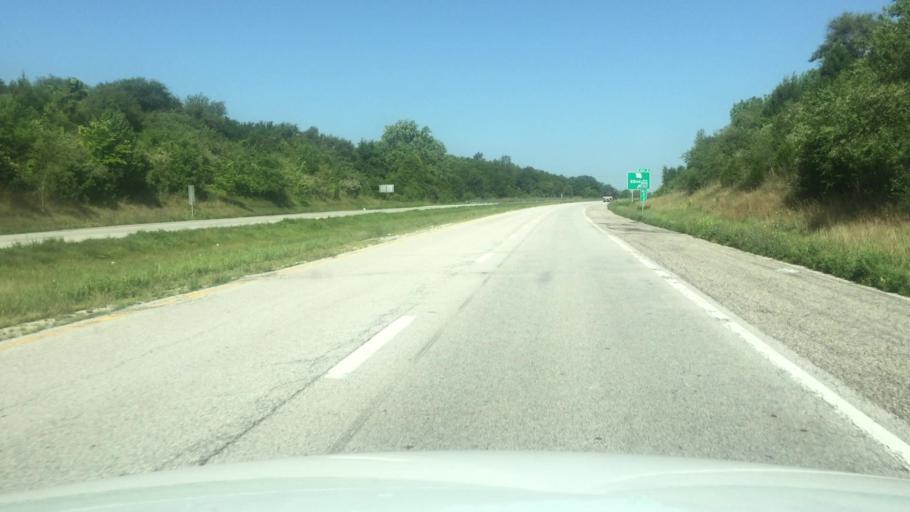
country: US
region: Missouri
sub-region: Buchanan County
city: Saint Joseph
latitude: 39.7185
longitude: -94.8264
